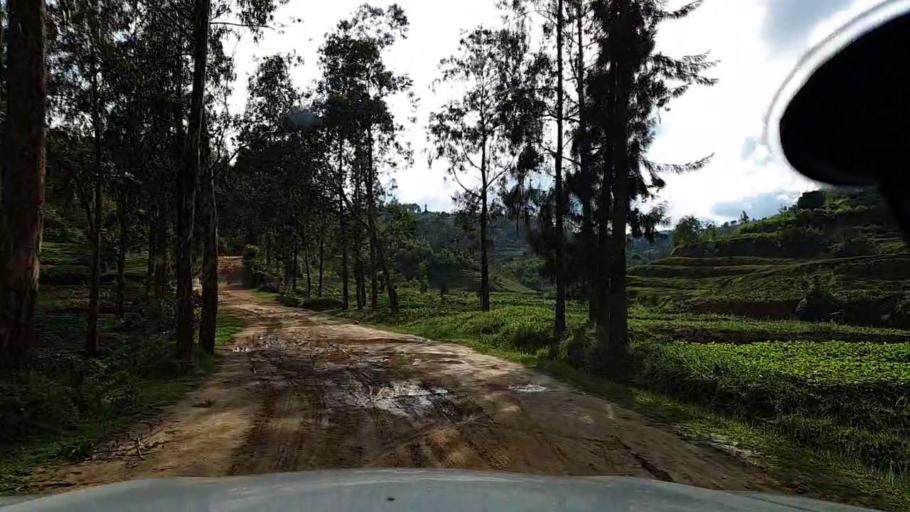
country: RW
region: Southern Province
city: Gitarama
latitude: -2.1673
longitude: 29.5575
